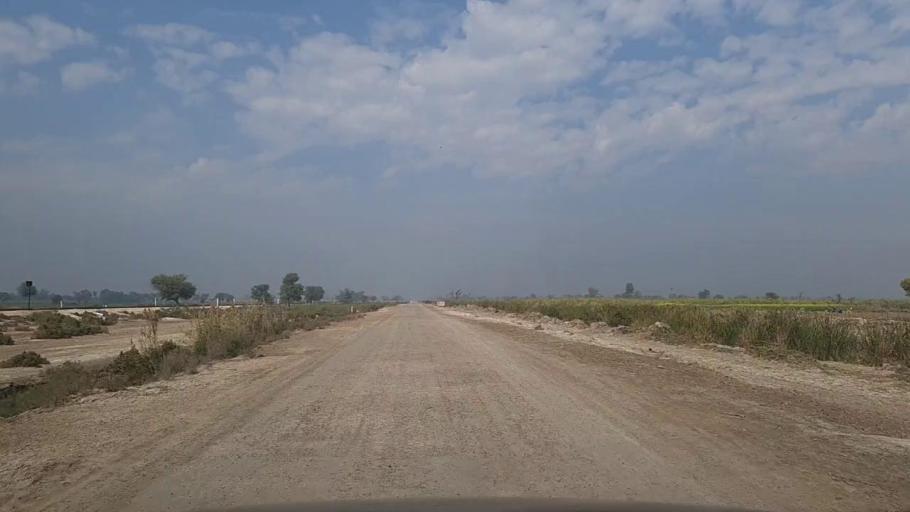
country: PK
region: Sindh
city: Daur
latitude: 26.3737
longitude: 68.3576
